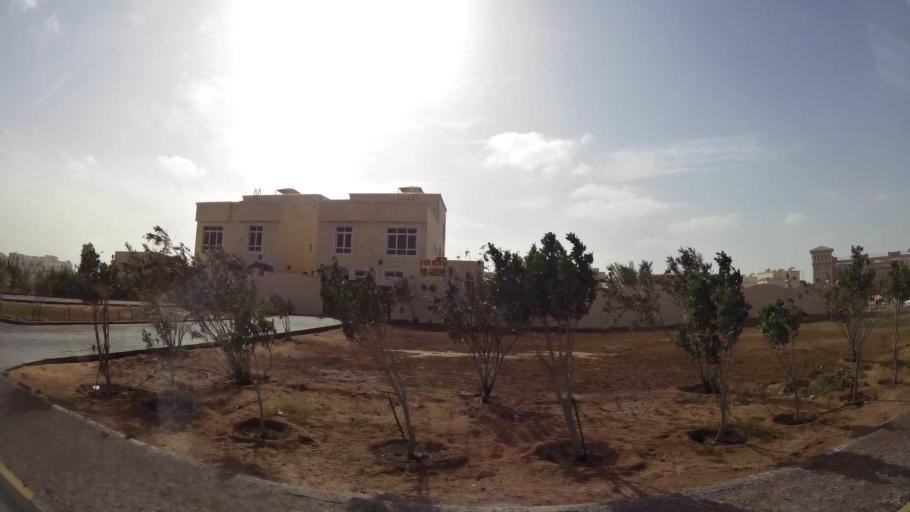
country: AE
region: Abu Dhabi
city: Abu Dhabi
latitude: 24.4297
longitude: 54.5993
